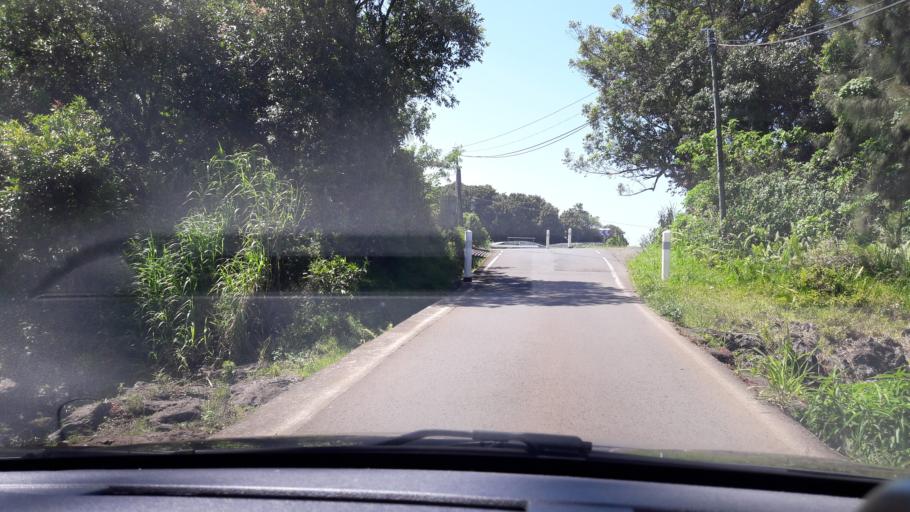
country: RE
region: Reunion
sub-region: Reunion
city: Saint-Benoit
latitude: -21.0876
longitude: 55.7000
